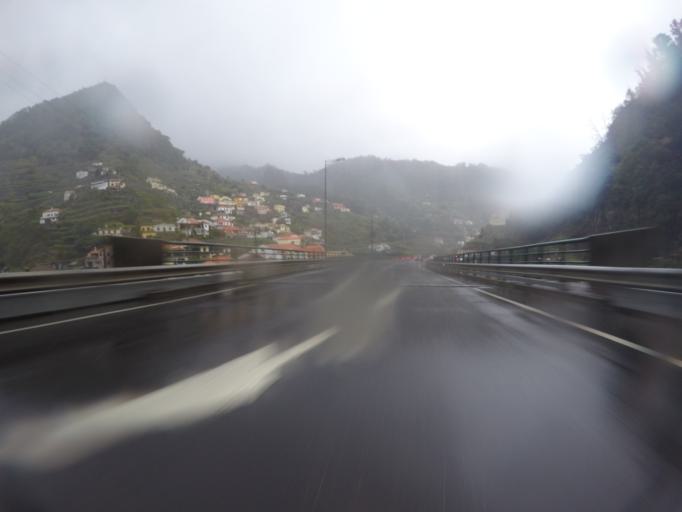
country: PT
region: Madeira
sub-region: Machico
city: Machico
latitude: 32.7345
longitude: -16.7961
